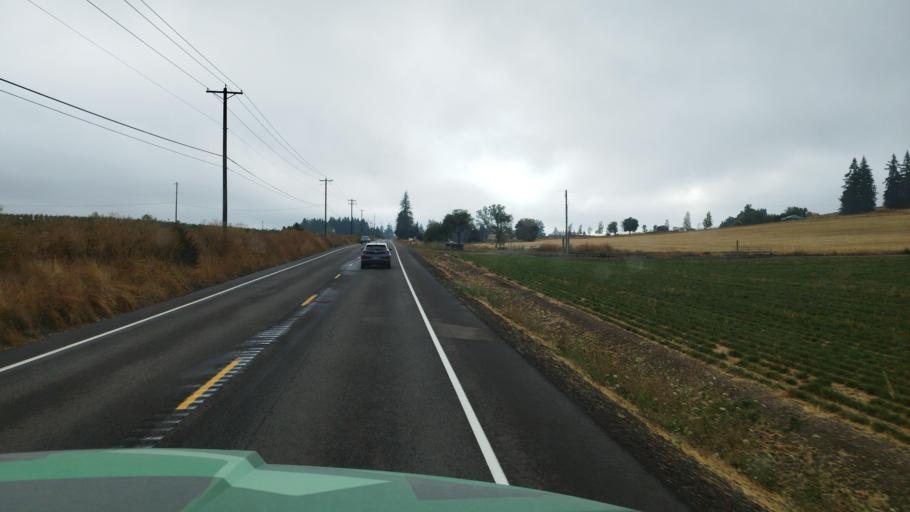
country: US
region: Oregon
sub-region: Yamhill County
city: Yamhill
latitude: 45.3254
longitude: -123.1801
